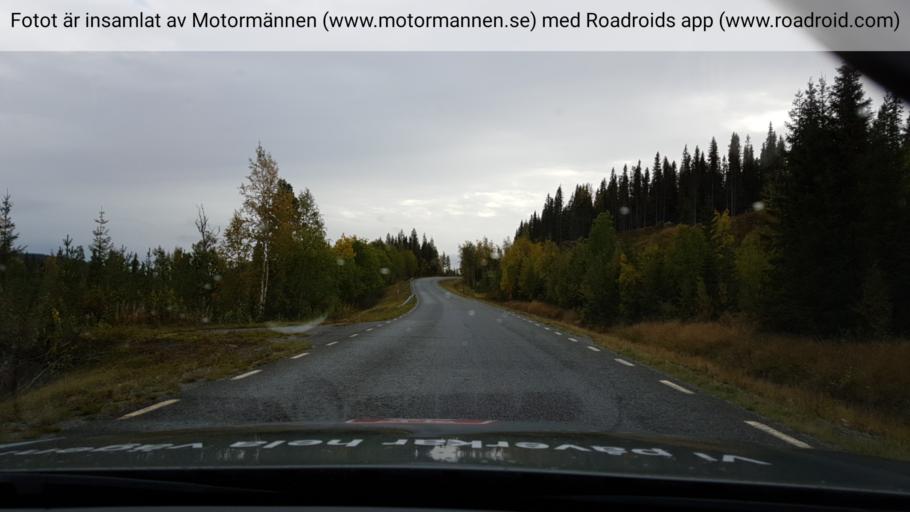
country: SE
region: Vaesterbotten
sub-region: Vilhelmina Kommun
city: Sjoberg
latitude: 64.9173
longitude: 15.8703
